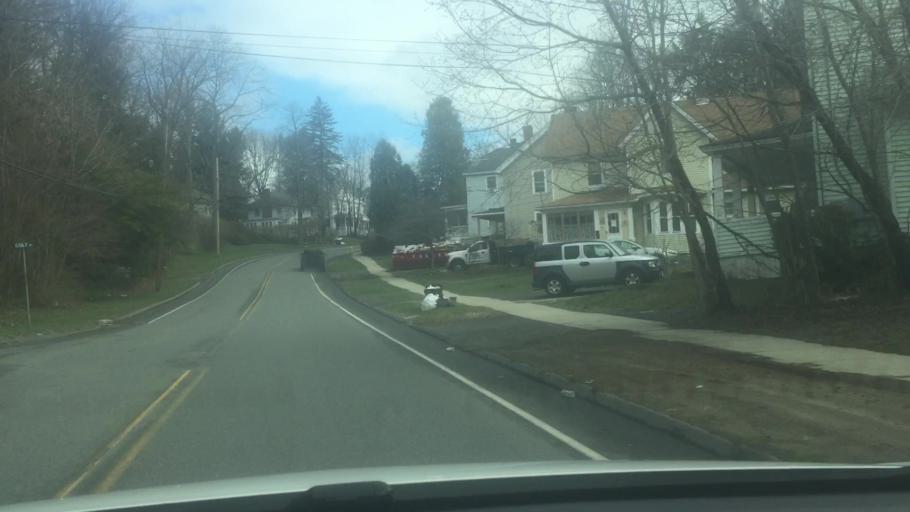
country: US
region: Massachusetts
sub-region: Berkshire County
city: Pittsfield
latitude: 42.4397
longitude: -73.2510
